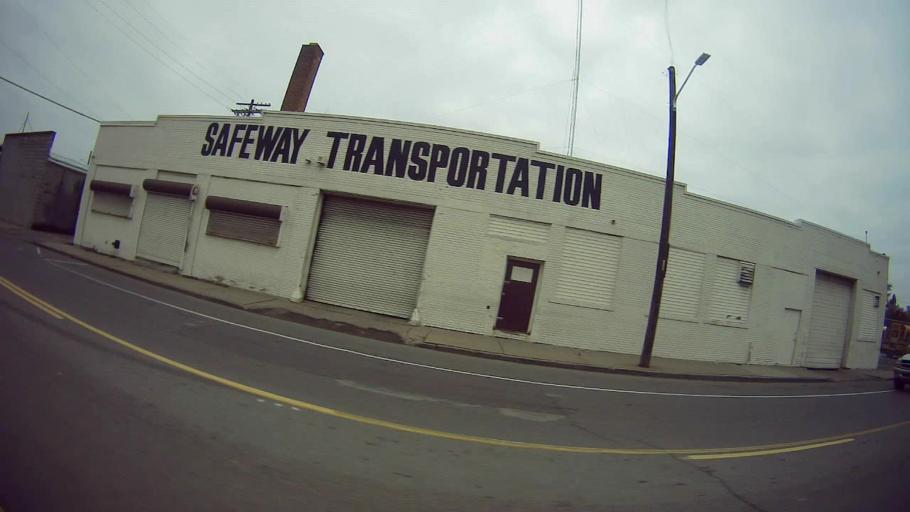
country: US
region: Michigan
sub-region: Wayne County
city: Hamtramck
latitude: 42.4161
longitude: -83.0618
